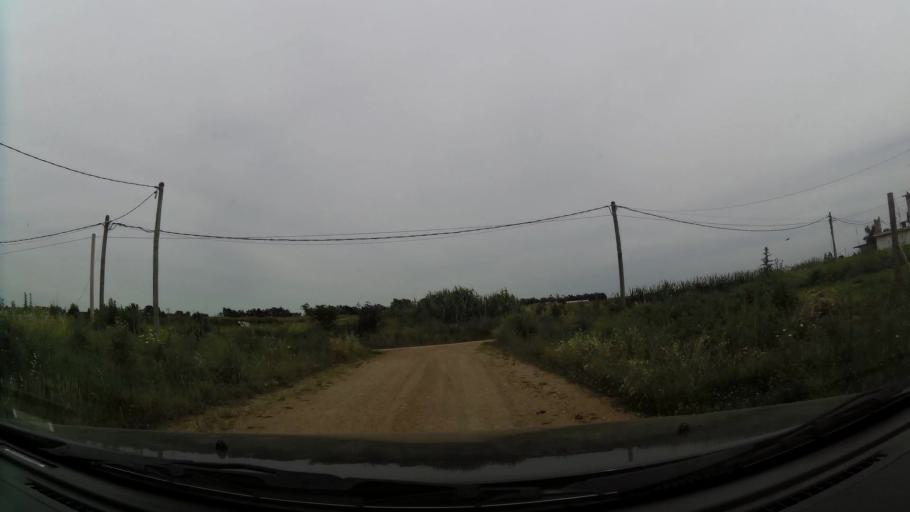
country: UY
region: Canelones
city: Las Piedras
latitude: -34.7378
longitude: -56.2349
